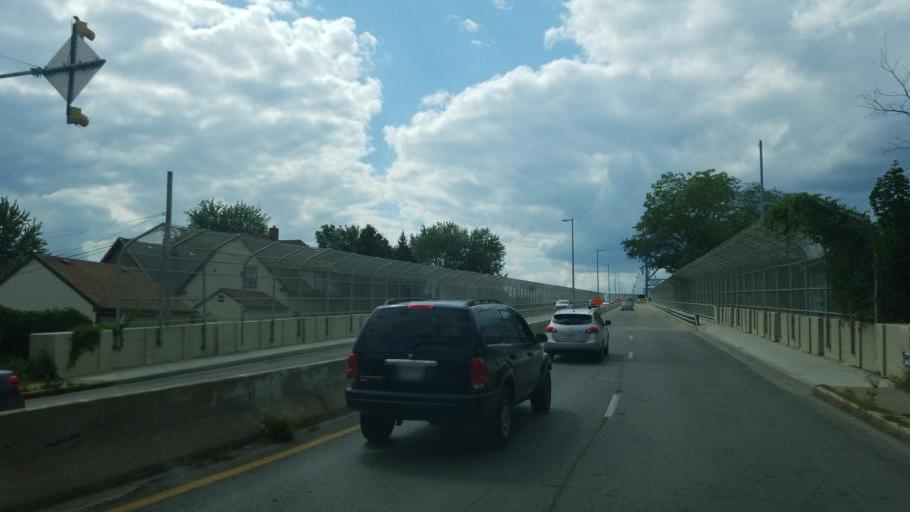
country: US
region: Ohio
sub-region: Lucas County
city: Toledo
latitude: 41.6409
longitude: -83.5267
